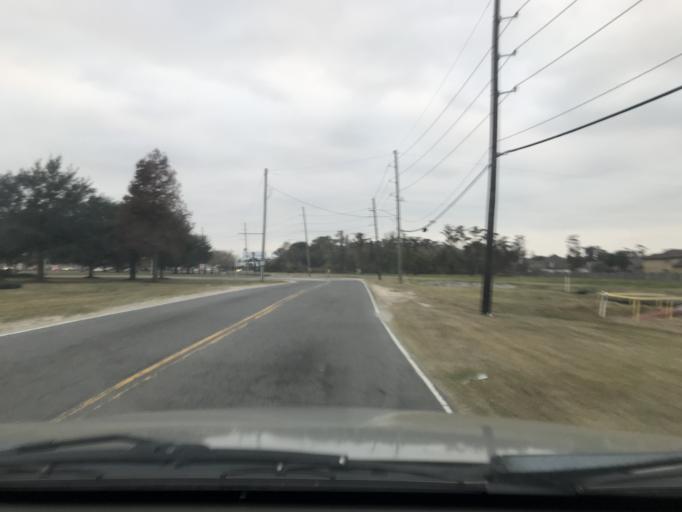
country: US
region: Louisiana
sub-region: Jefferson Parish
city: Woodmere
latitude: 29.8705
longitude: -90.0739
